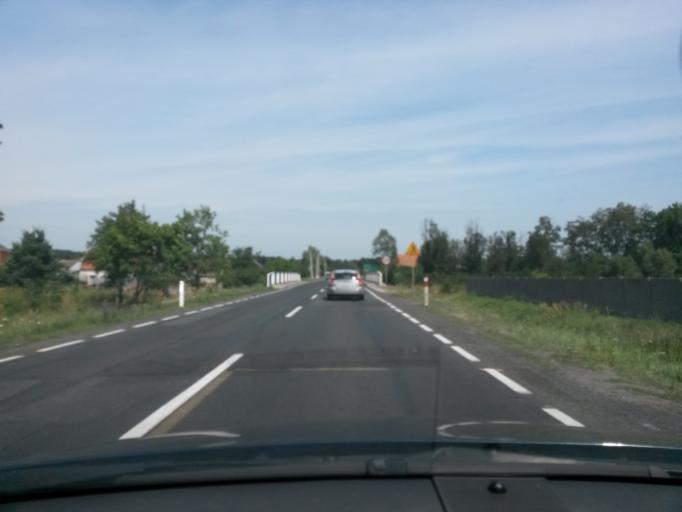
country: PL
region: Lower Silesian Voivodeship
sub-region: Powiat legnicki
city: Prochowice
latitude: 51.2866
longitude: 16.3472
